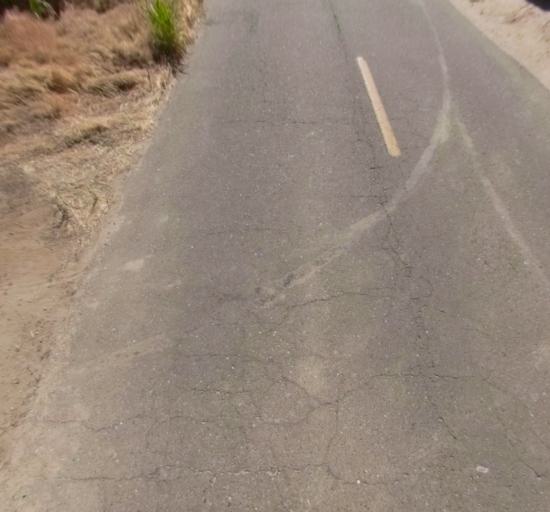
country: US
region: California
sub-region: Madera County
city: Madera
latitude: 36.9456
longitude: -120.1036
